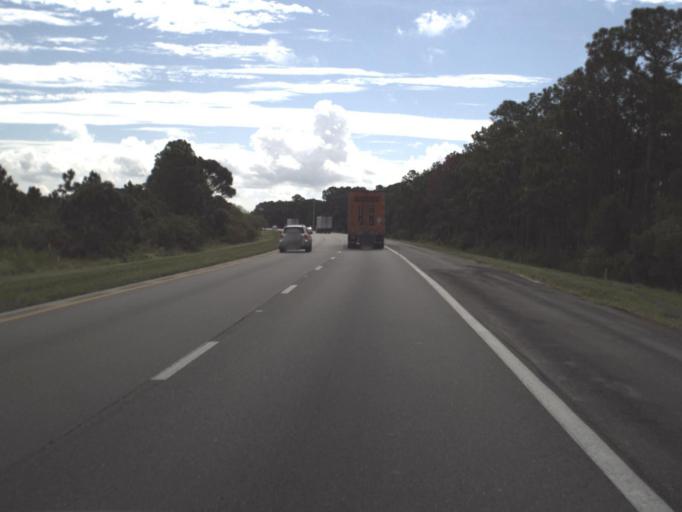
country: US
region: Florida
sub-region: Sarasota County
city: Warm Mineral Springs
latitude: 27.1008
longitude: -82.2859
